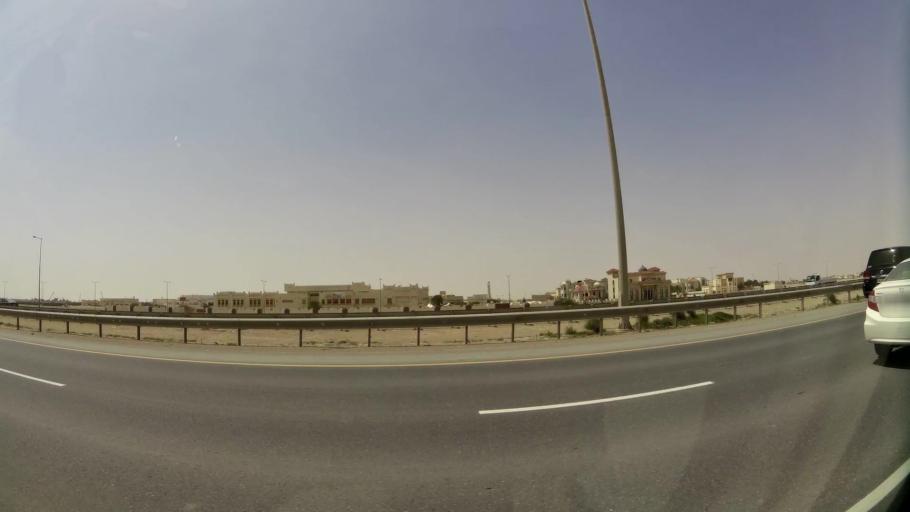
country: QA
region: Baladiyat Umm Salal
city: Umm Salal Muhammad
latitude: 25.4225
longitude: 51.4189
